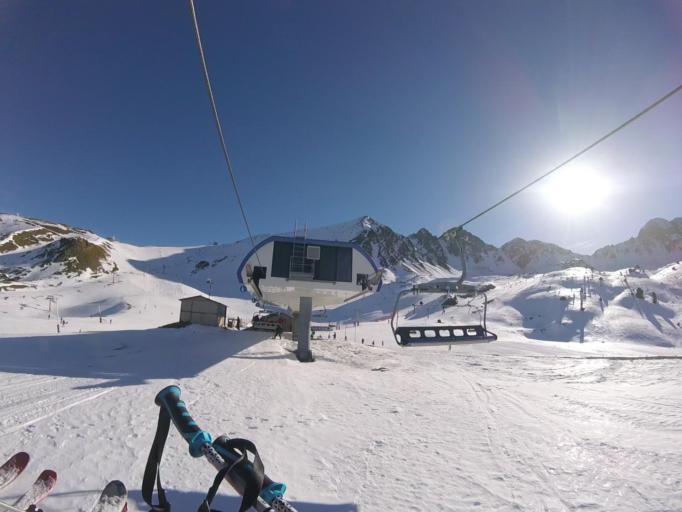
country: AD
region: Encamp
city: Pas de la Casa
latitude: 42.5262
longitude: 1.7122
